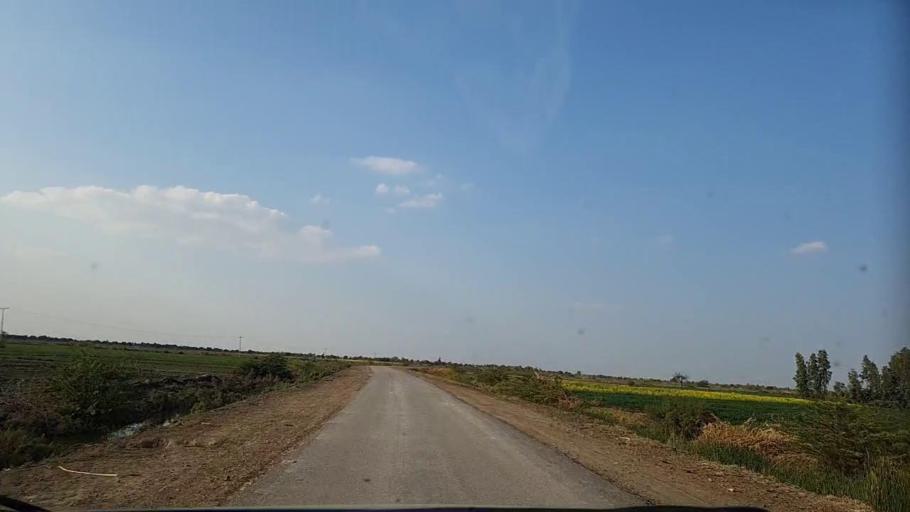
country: PK
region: Sindh
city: Pithoro
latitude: 25.7146
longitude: 69.2199
